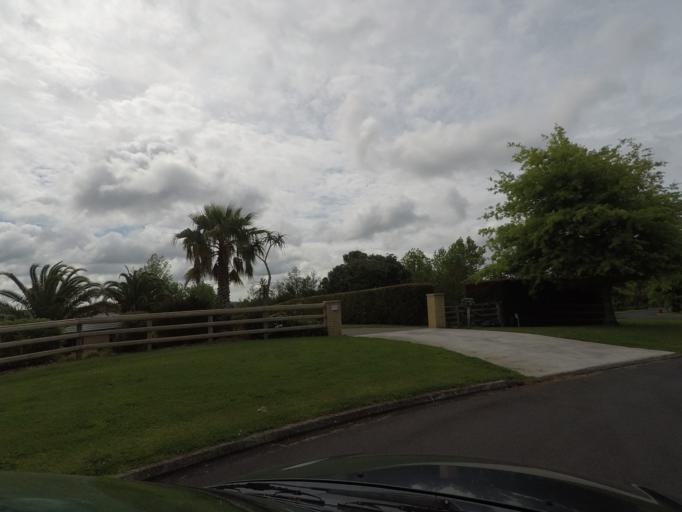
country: NZ
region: Auckland
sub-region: Auckland
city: Muriwai Beach
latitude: -36.7643
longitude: 174.5703
